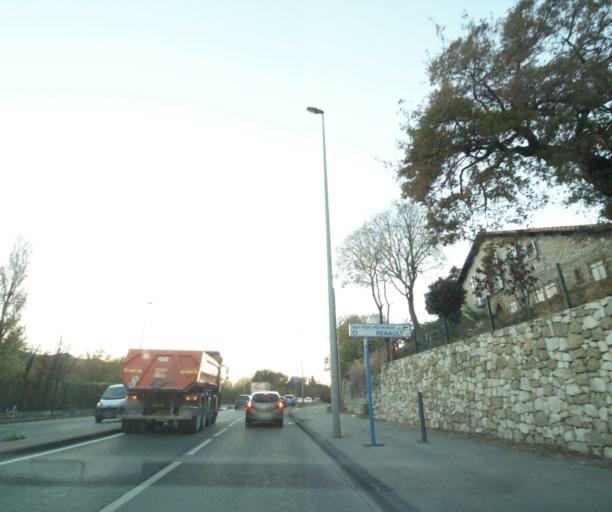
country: FR
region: Provence-Alpes-Cote d'Azur
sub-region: Departement des Bouches-du-Rhone
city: La Penne-sur-Huveaune
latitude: 43.2883
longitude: 5.5031
